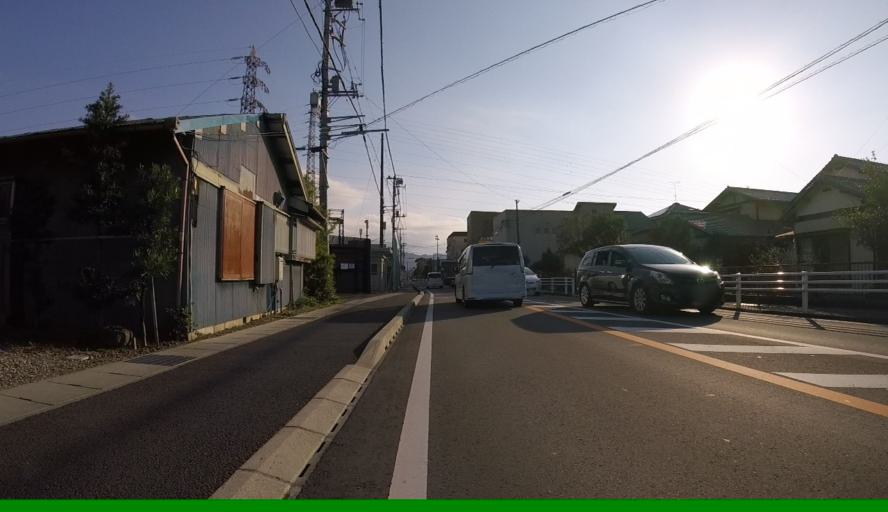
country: JP
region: Shizuoka
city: Mishima
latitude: 35.1040
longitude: 138.9044
